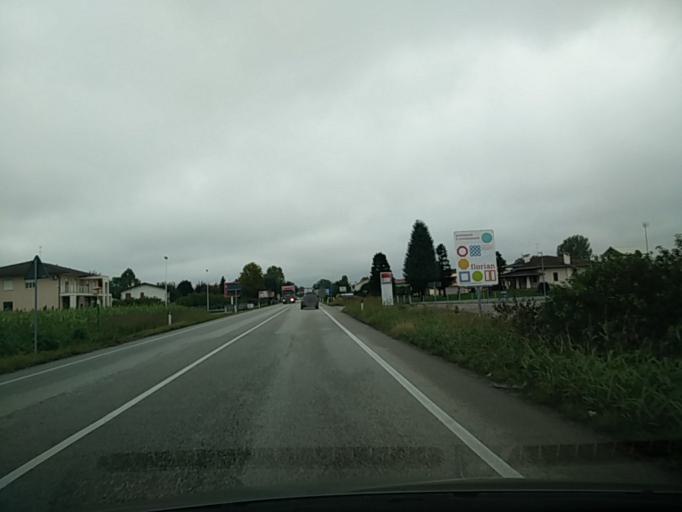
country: IT
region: Veneto
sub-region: Provincia di Treviso
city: Vedelago
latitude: 45.6850
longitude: 12.0015
